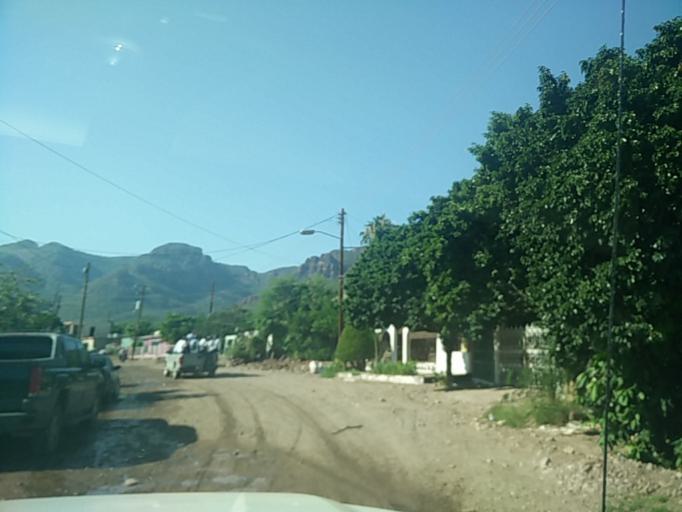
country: MX
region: Sonora
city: Heroica Guaymas
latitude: 27.9367
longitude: -110.8805
